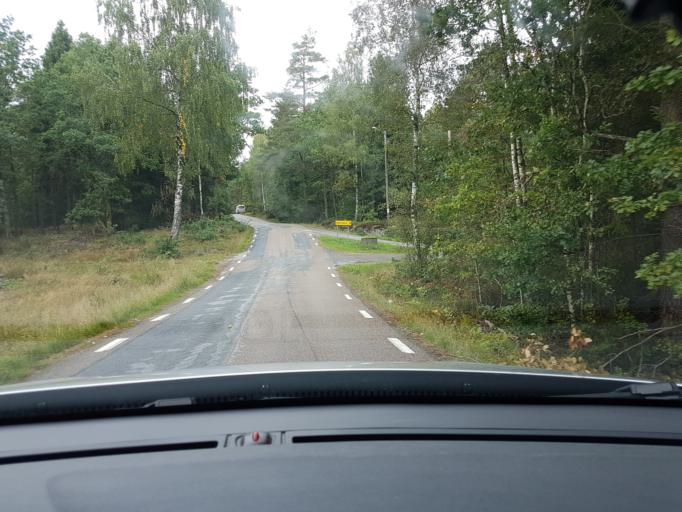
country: SE
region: Vaestra Goetaland
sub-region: Ale Kommun
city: Alvangen
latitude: 57.9030
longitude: 12.1783
